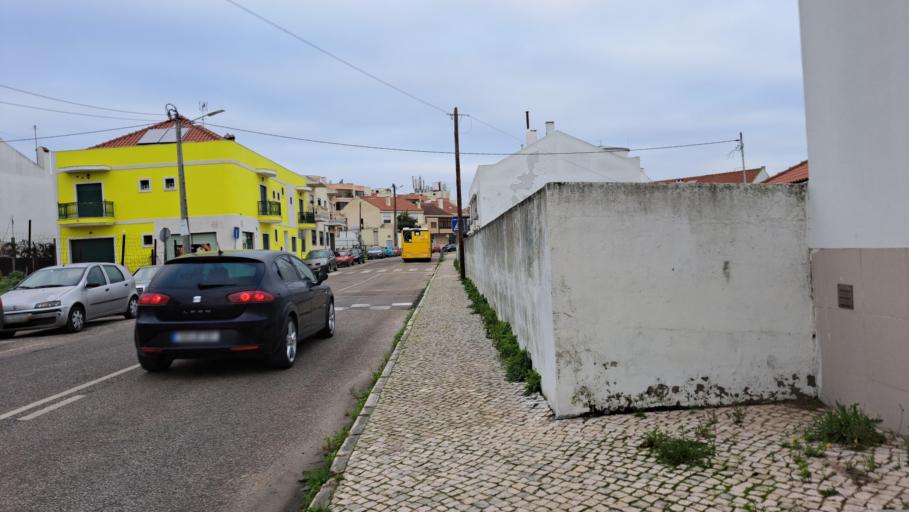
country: PT
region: Setubal
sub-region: Moita
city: Alhos Vedros
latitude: 38.6519
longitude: -9.0462
